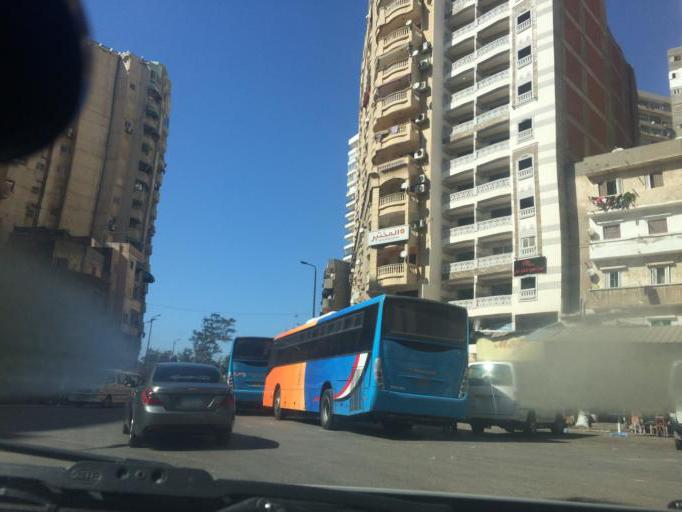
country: EG
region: Alexandria
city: Alexandria
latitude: 31.2798
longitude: 30.0122
